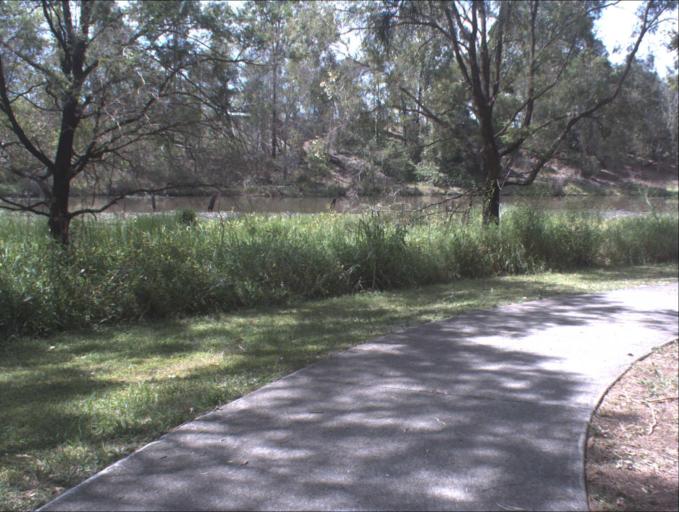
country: AU
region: Queensland
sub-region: Logan
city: Slacks Creek
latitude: -27.6715
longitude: 153.1553
